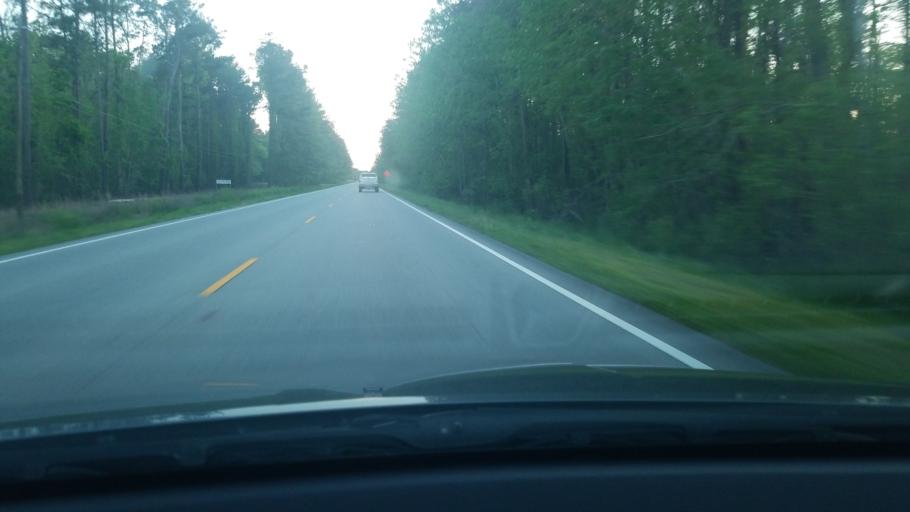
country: US
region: North Carolina
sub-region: Craven County
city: Vanceboro
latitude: 35.2442
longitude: -77.0950
